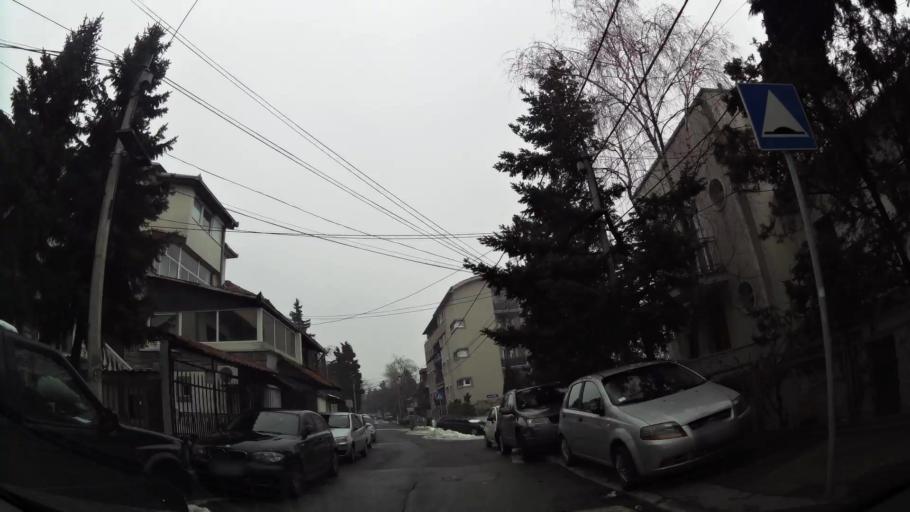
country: RS
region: Central Serbia
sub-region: Belgrade
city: Vozdovac
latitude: 44.7789
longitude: 20.4775
